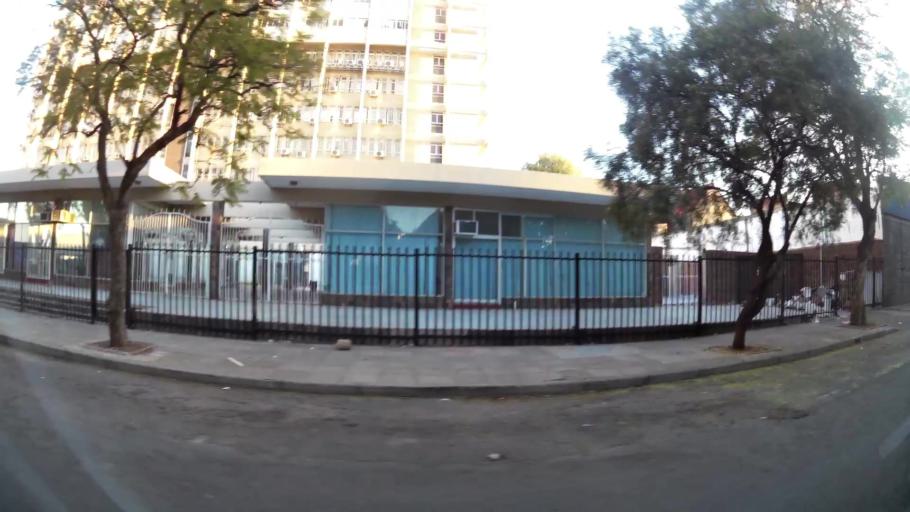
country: ZA
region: Northern Cape
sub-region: Frances Baard District Municipality
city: Kimberley
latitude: -28.7405
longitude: 24.7673
